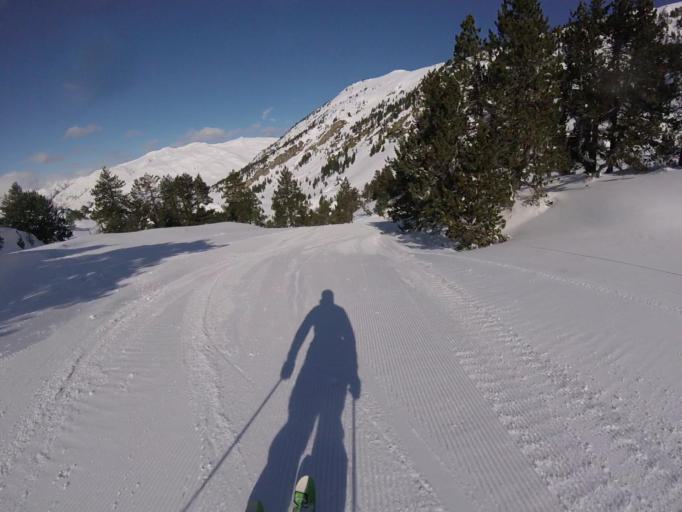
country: ES
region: Catalonia
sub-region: Provincia de Lleida
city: Espot
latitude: 42.7011
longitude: 0.9759
